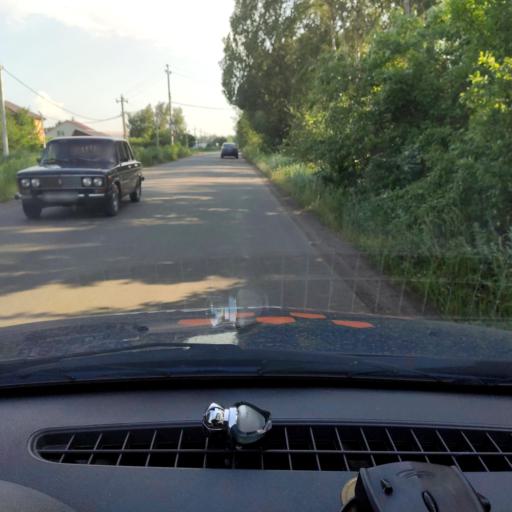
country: RU
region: Voronezj
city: Podkletnoye
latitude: 51.6046
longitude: 39.4300
